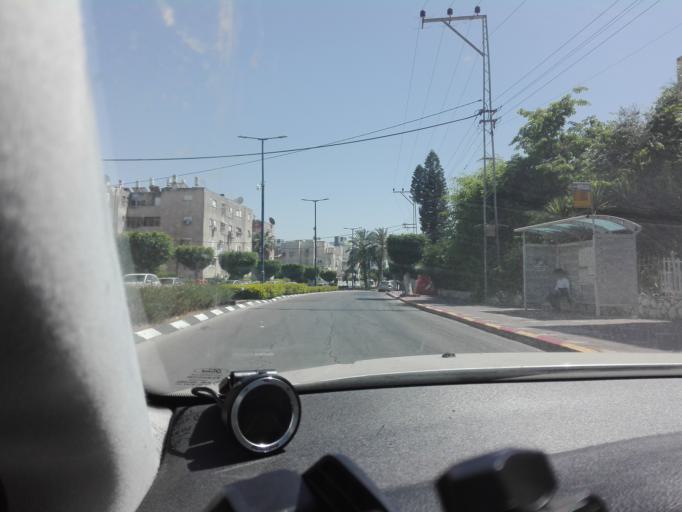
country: IL
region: Central District
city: Bene 'Ayish
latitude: 31.7322
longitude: 34.7402
